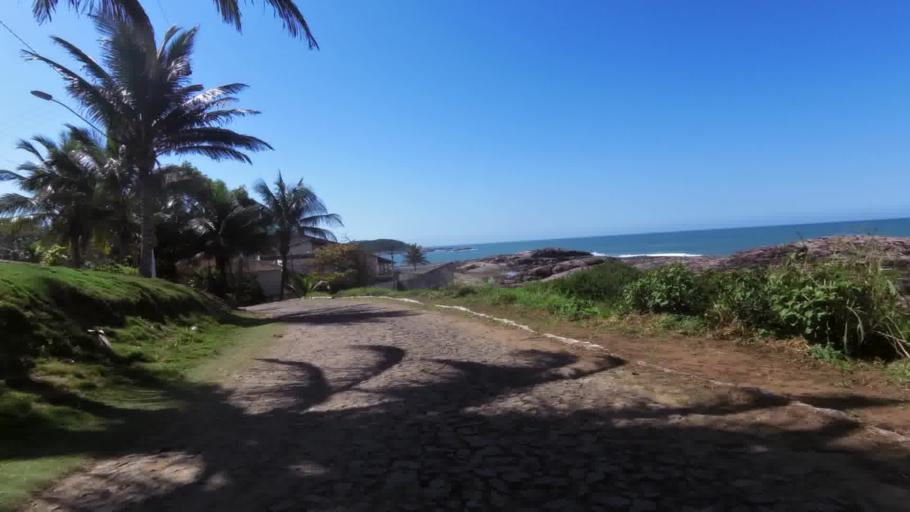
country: BR
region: Espirito Santo
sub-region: Guarapari
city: Guarapari
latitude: -20.7424
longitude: -40.5353
